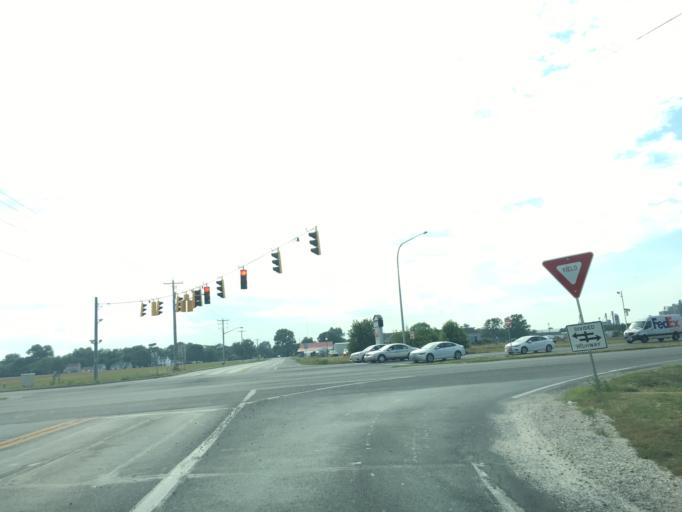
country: US
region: Delaware
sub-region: Sussex County
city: Bridgeville
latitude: 38.7491
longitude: -75.5927
